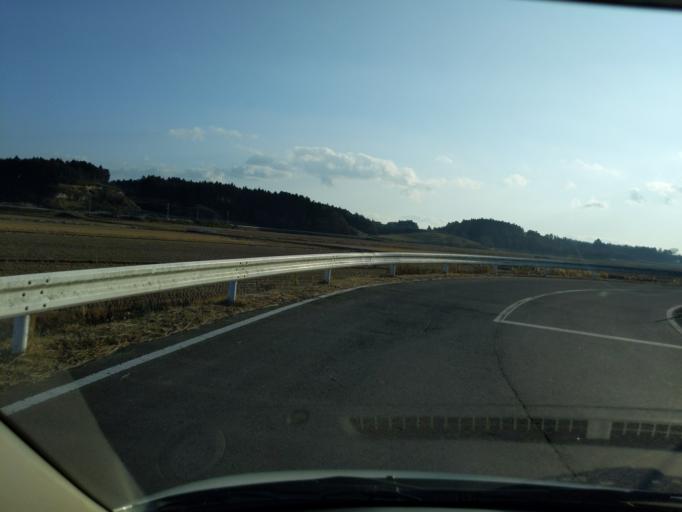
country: JP
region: Miyagi
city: Wakuya
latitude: 38.7109
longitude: 141.1309
